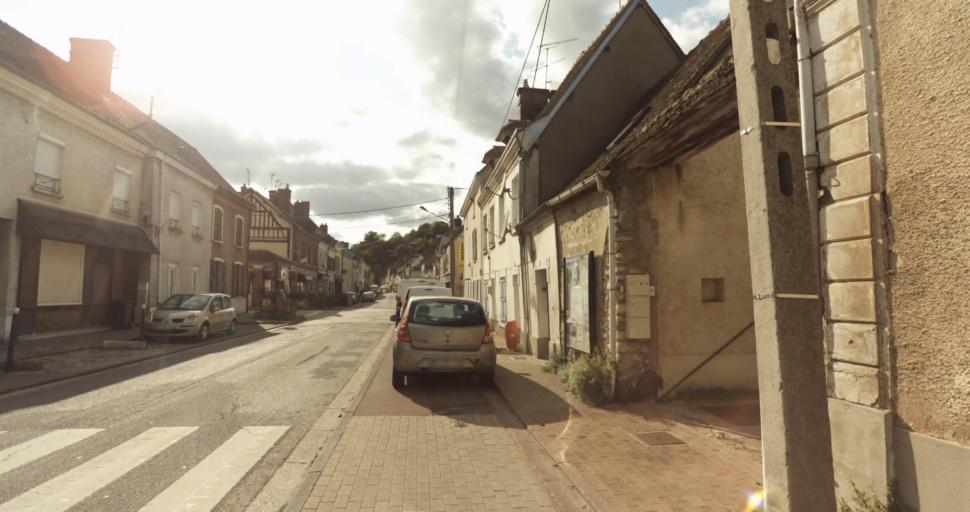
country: FR
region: Haute-Normandie
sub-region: Departement de l'Eure
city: Ivry-la-Bataille
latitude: 48.8831
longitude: 1.4625
